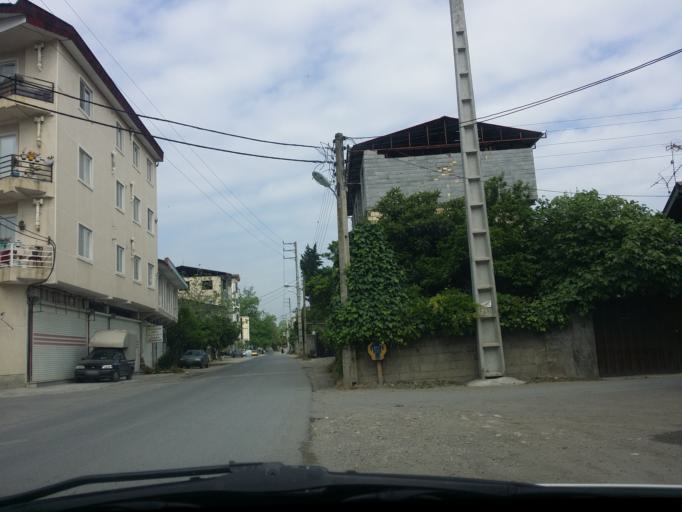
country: IR
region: Mazandaran
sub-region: Nowshahr
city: Nowshahr
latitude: 36.6264
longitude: 51.4882
